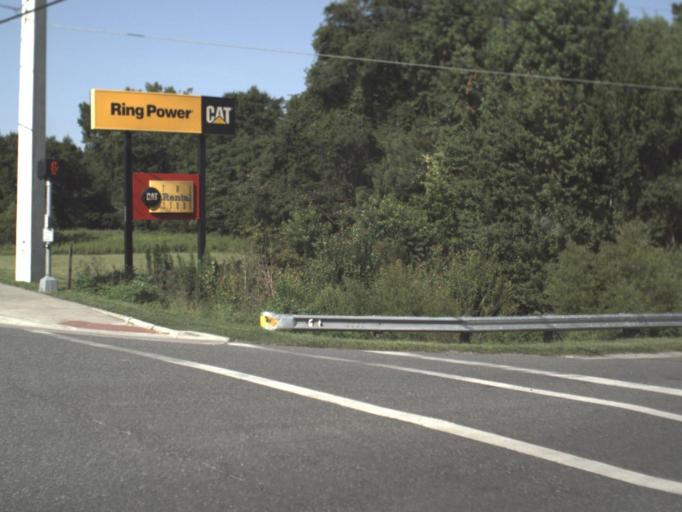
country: US
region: Florida
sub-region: Columbia County
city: Lake City
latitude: 30.1210
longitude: -82.6540
